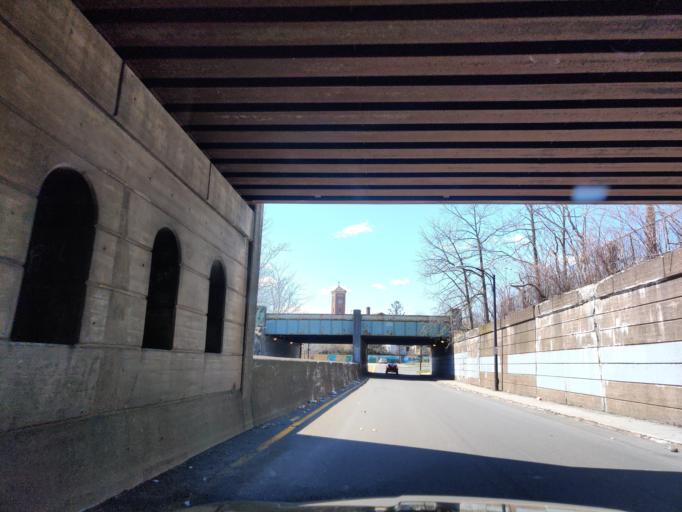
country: US
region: New York
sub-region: Erie County
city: Kenmore
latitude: 42.9359
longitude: -78.8973
